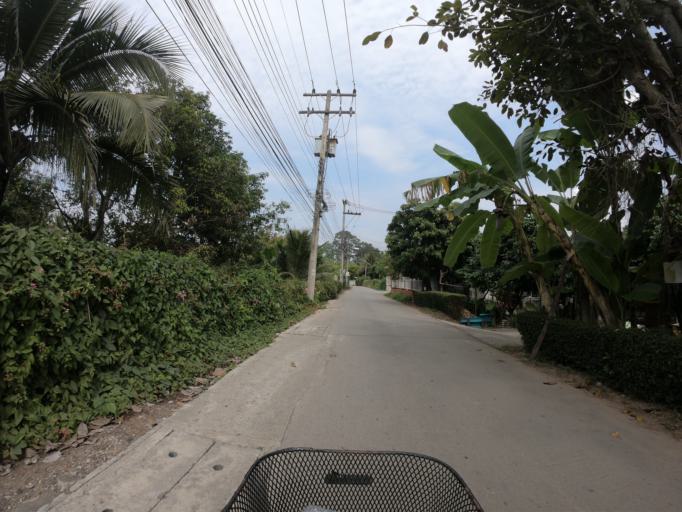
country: TH
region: Chiang Mai
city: Saraphi
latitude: 18.7092
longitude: 99.0385
